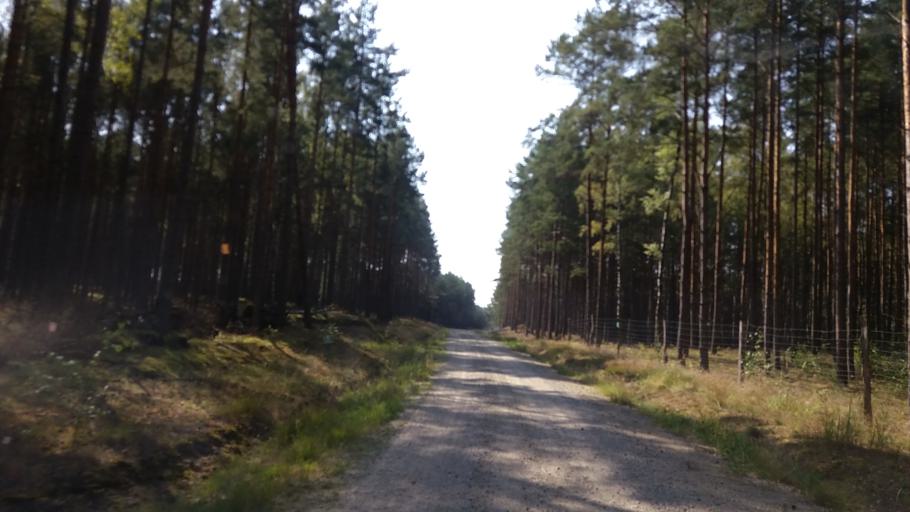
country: PL
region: West Pomeranian Voivodeship
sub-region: Powiat drawski
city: Kalisz Pomorski
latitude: 53.1918
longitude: 15.9625
